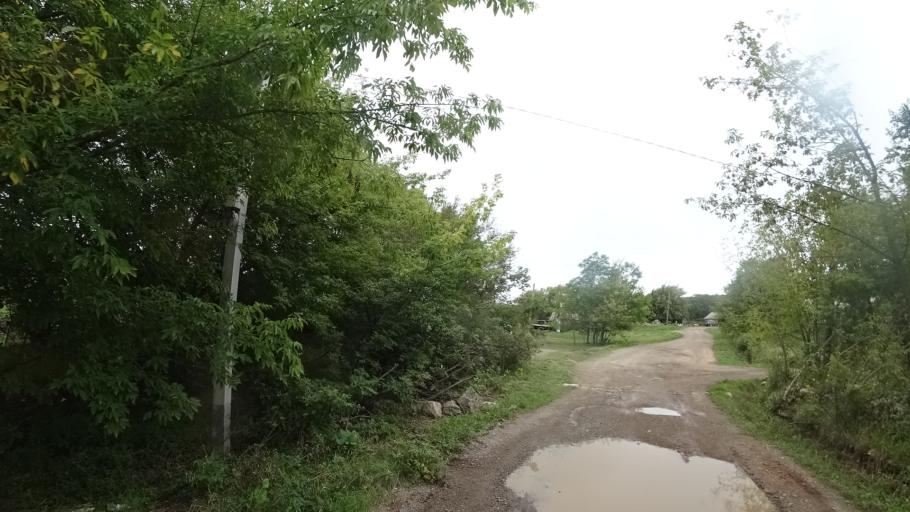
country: RU
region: Primorskiy
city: Monastyrishche
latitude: 44.2658
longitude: 132.4588
